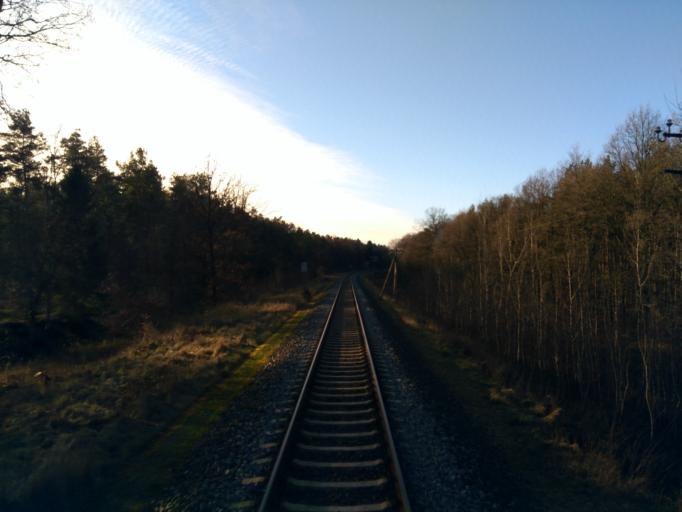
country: DE
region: Lower Saxony
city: Soltau
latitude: 52.9842
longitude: 9.9196
